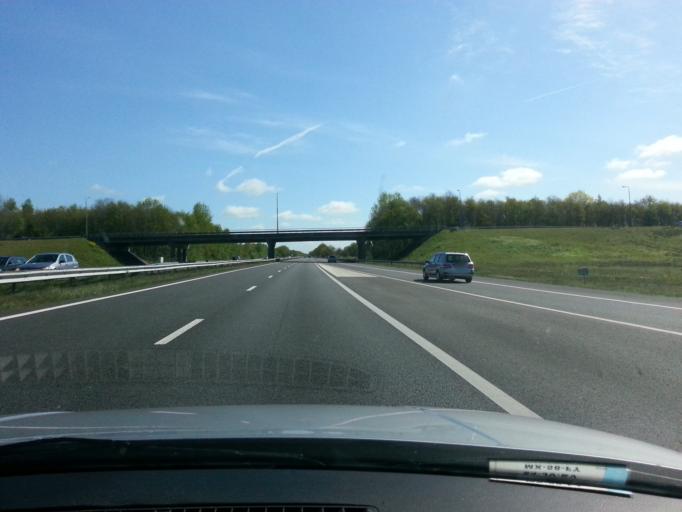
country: NL
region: Friesland
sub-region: Gemeente Smallingerland
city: Drachten
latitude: 53.0894
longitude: 6.0848
